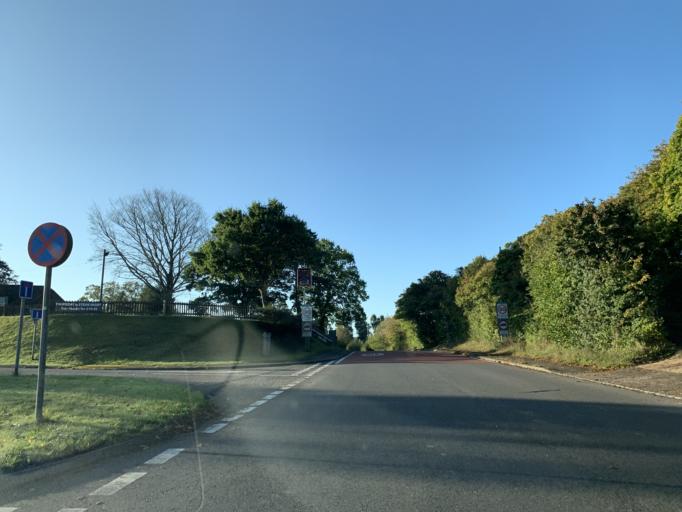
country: GB
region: England
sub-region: Wiltshire
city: Whiteparish
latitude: 50.9811
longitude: -1.6375
